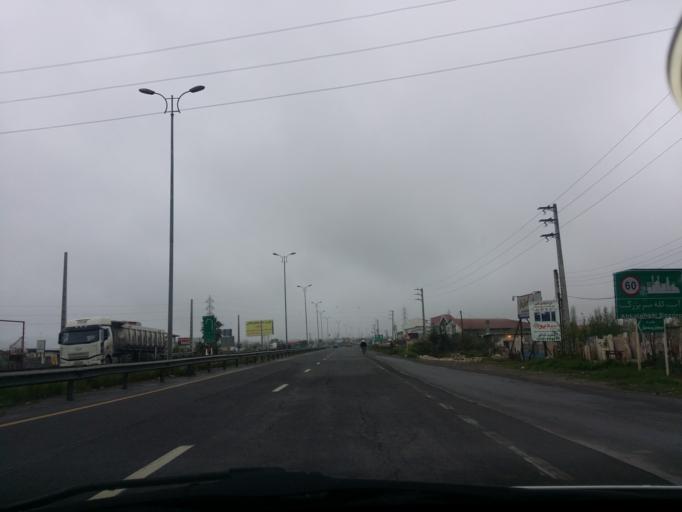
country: IR
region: Mazandaran
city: Tonekabon
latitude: 36.7963
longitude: 50.9060
